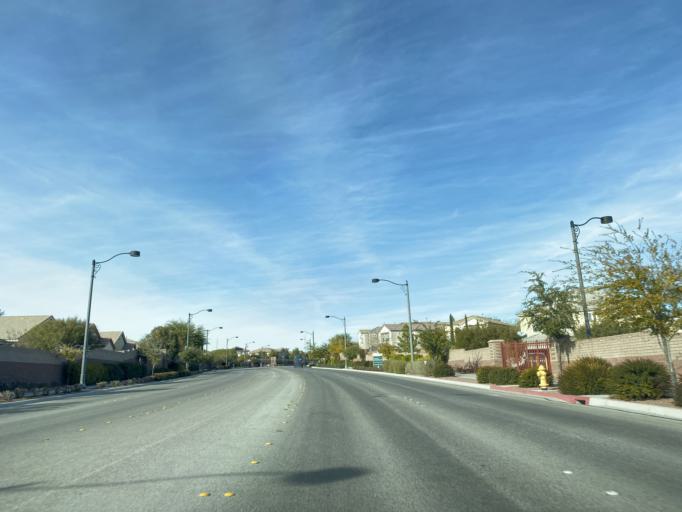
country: US
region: Nevada
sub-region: Clark County
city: Summerlin South
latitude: 36.3023
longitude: -115.3201
